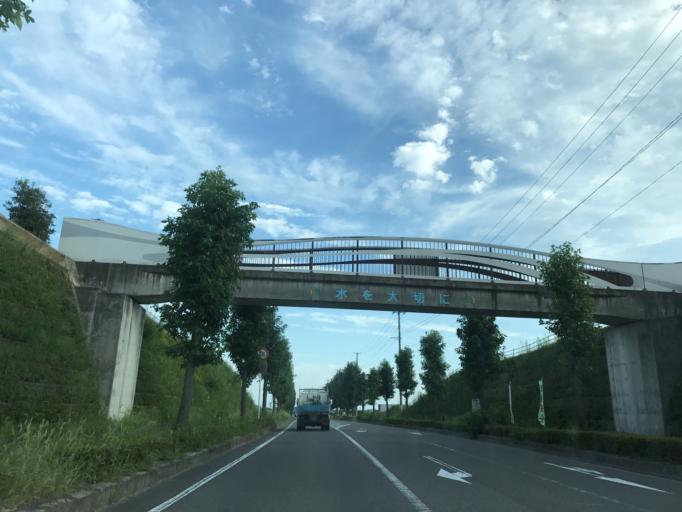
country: JP
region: Fukushima
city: Sukagawa
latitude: 37.3384
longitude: 140.3381
